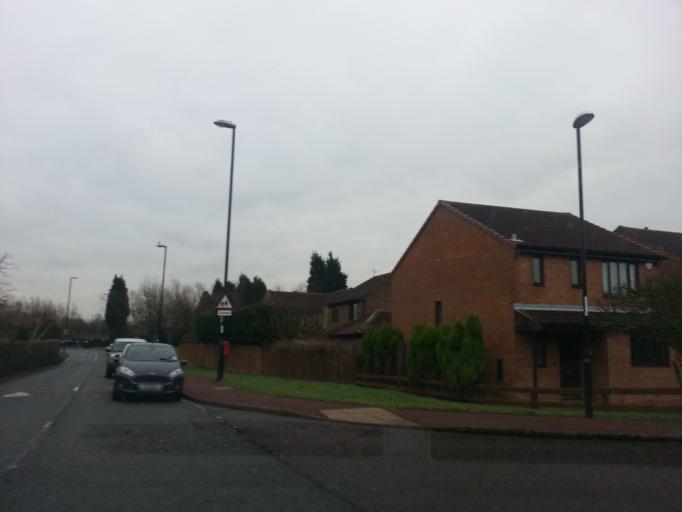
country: GB
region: England
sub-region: County Durham
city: Chester-le-Street
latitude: 54.8788
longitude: -1.5536
